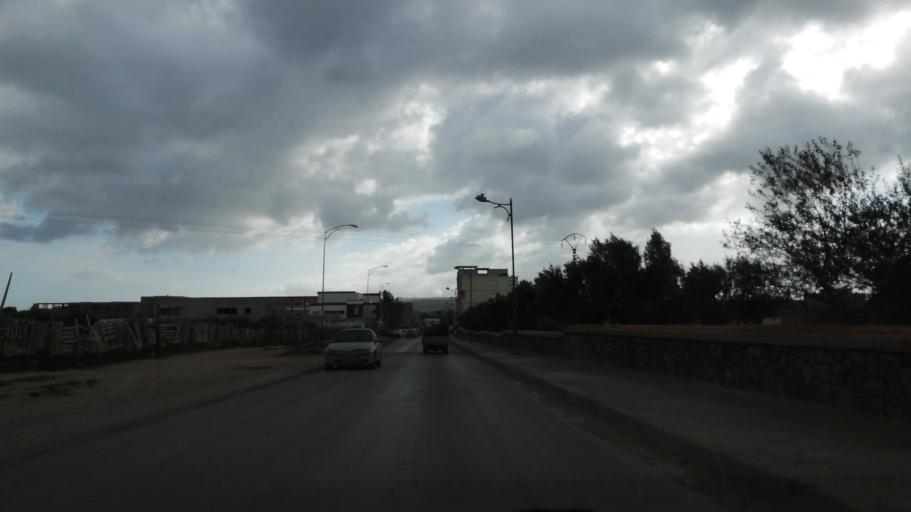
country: DZ
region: Oran
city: Sidi ech Chahmi
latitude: 35.6578
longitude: -0.5301
